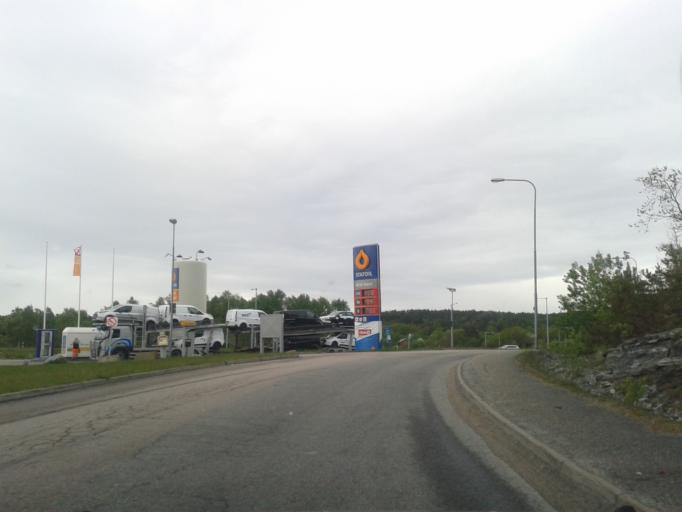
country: SE
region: Vaestra Goetaland
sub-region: Stenungsunds Kommun
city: Stora Hoga
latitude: 58.0241
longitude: 11.8482
